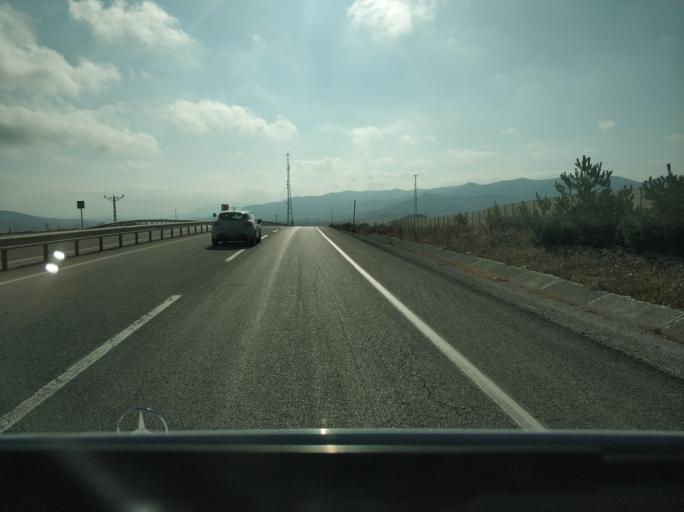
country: TR
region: Sivas
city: Yildizeli
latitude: 39.8351
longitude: 36.4100
